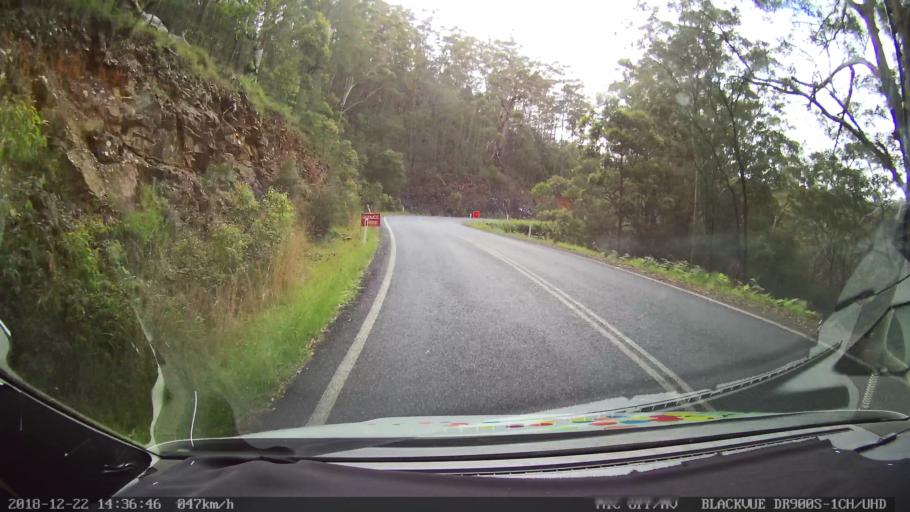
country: AU
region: New South Wales
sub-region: Bellingen
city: Dorrigo
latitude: -30.1304
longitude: 152.6039
